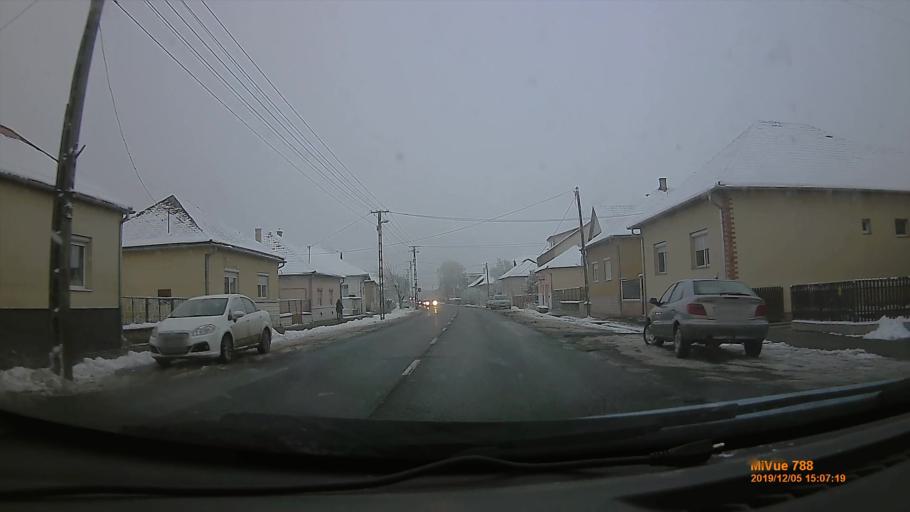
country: HU
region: Szabolcs-Szatmar-Bereg
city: Rakamaz
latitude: 48.1212
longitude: 21.4711
